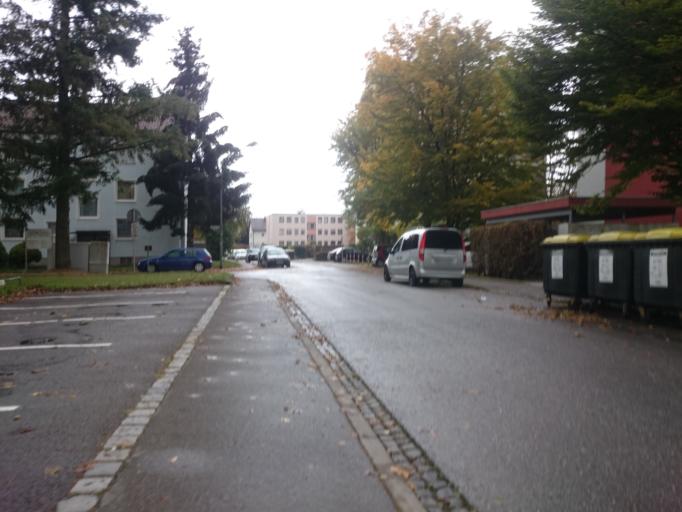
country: DE
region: Bavaria
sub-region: Swabia
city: Gersthofen
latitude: 48.4287
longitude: 10.8684
